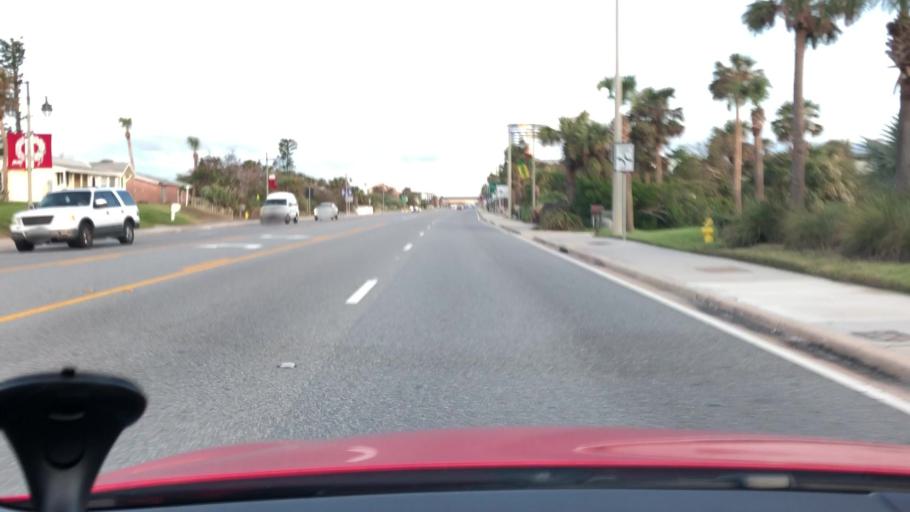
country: US
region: Florida
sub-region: Volusia County
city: Daytona Beach Shores
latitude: 29.1753
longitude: -80.9825
